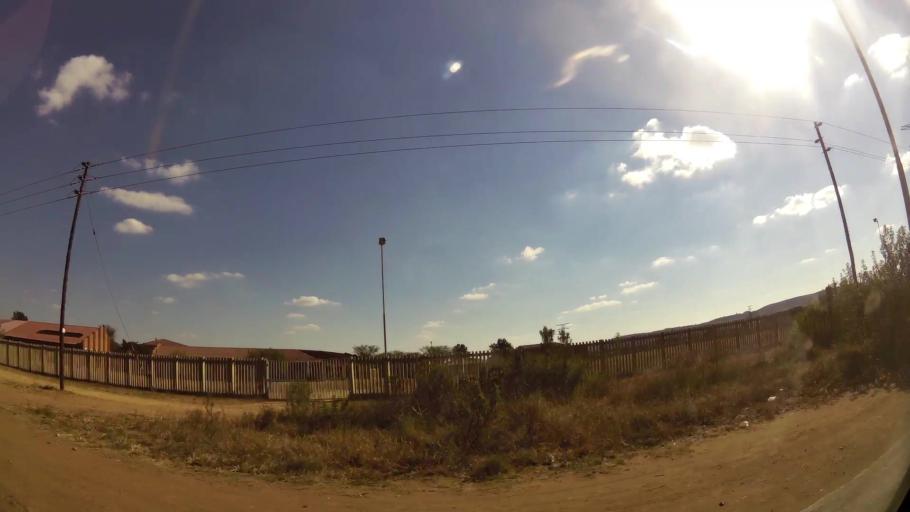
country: ZA
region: Gauteng
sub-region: City of Tshwane Metropolitan Municipality
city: Cullinan
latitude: -25.7199
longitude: 28.4014
